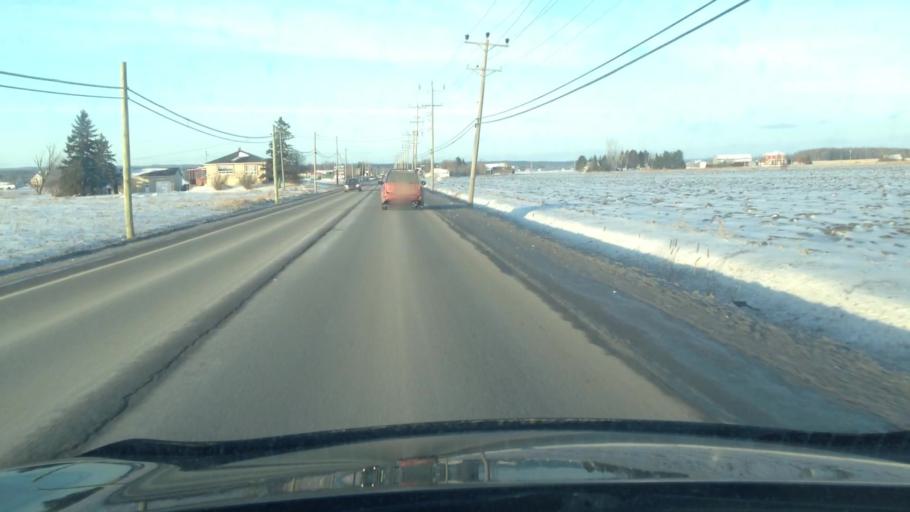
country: CA
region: Quebec
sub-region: Lanaudiere
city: Saint-Lin-Laurentides
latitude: 45.8725
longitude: -73.7572
